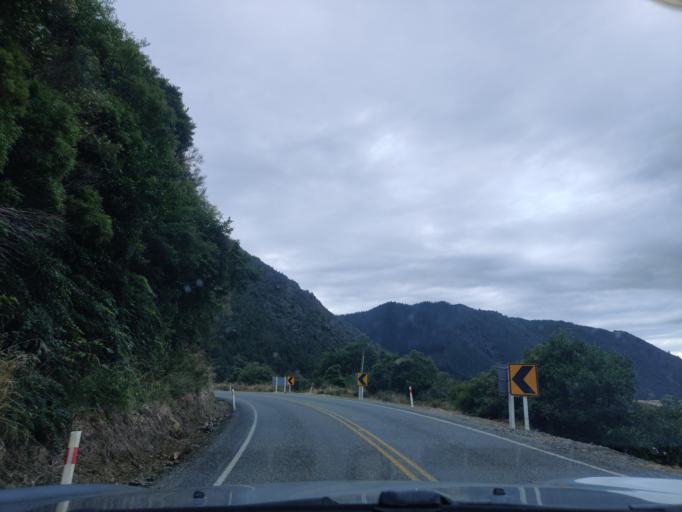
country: NZ
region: Tasman
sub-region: Tasman District
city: Wakefield
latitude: -41.6989
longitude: 172.6250
